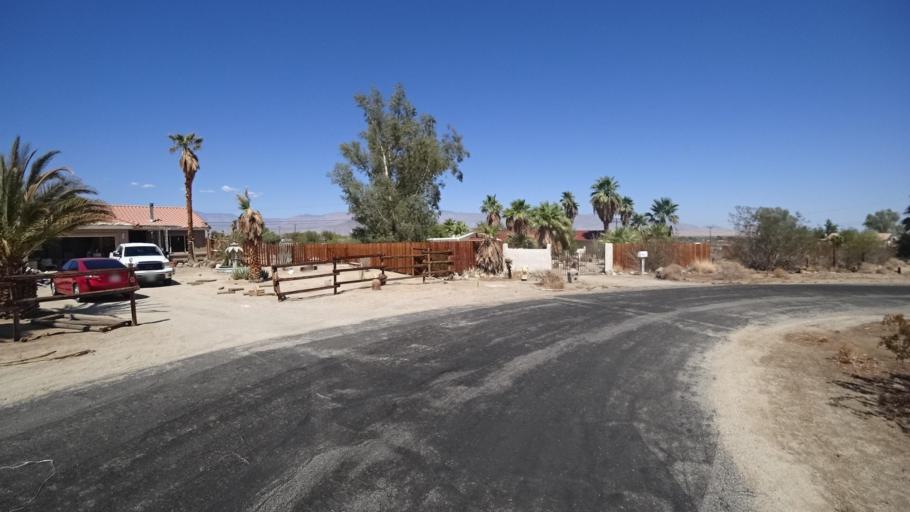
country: US
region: California
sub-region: San Diego County
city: Borrego Springs
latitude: 33.2274
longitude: -116.3723
